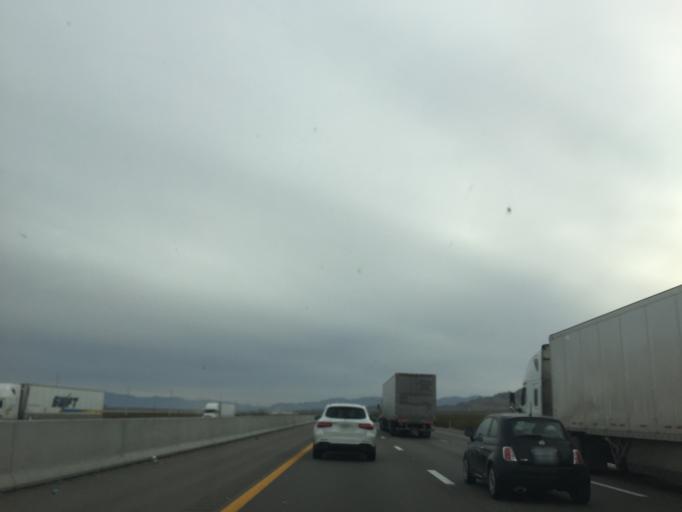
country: US
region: Nevada
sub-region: Clark County
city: Sandy Valley
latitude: 35.7041
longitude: -115.3692
